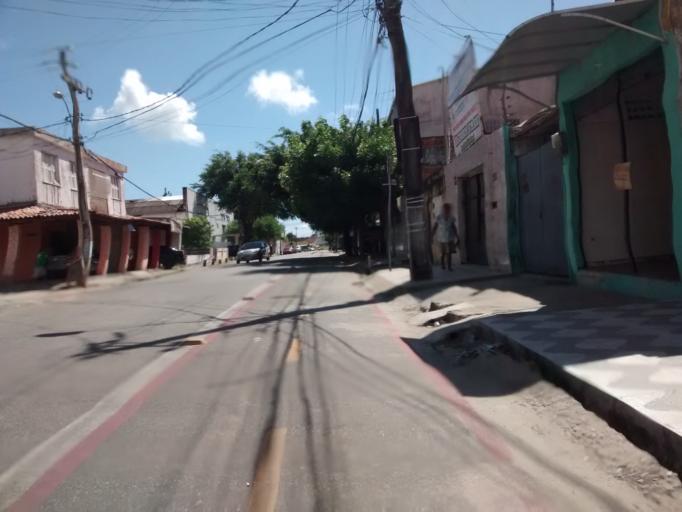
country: BR
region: Ceara
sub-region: Fortaleza
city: Fortaleza
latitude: -3.7220
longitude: -38.5502
